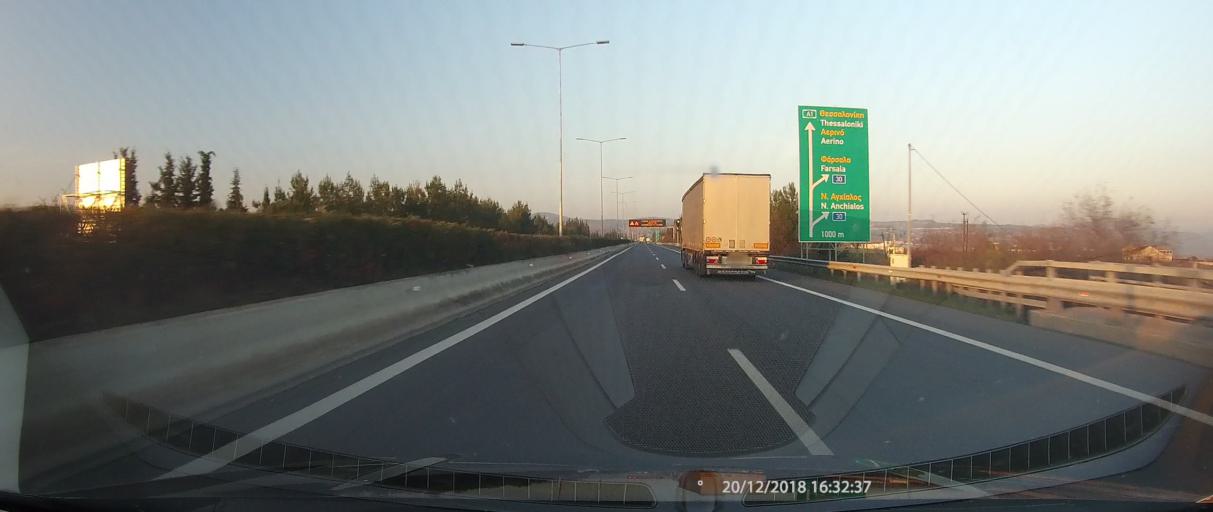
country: GR
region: Thessaly
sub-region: Nomos Magnisias
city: Evxinoupolis
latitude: 39.2482
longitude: 22.7347
